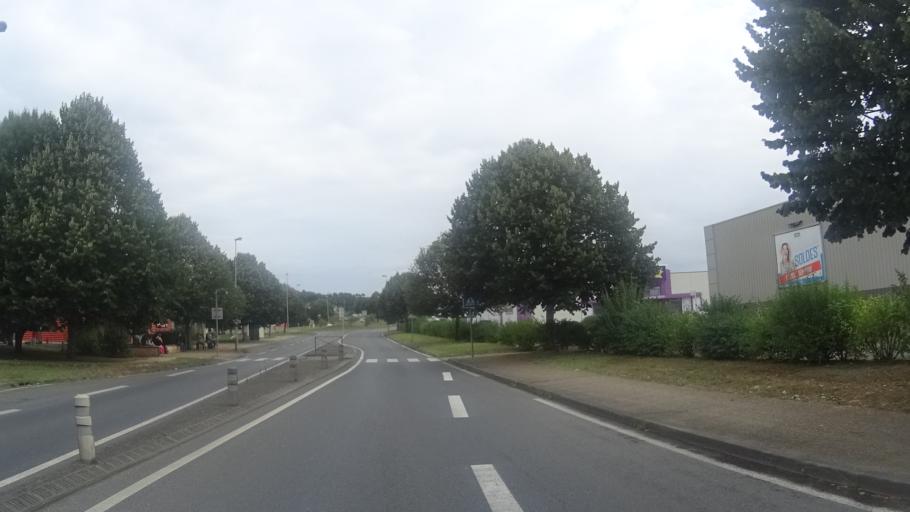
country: FR
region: Aquitaine
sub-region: Departement de la Dordogne
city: Chancelade
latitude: 45.1926
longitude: 0.6612
